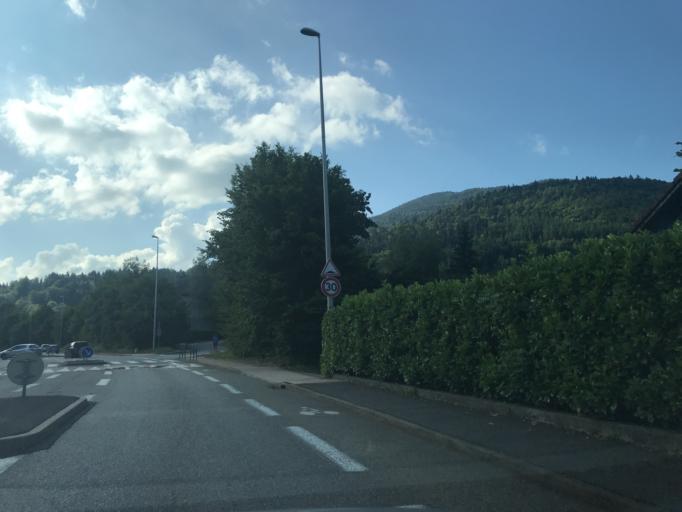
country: FR
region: Rhone-Alpes
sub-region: Departement de la Haute-Savoie
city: Villaz
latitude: 45.9224
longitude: 6.1756
